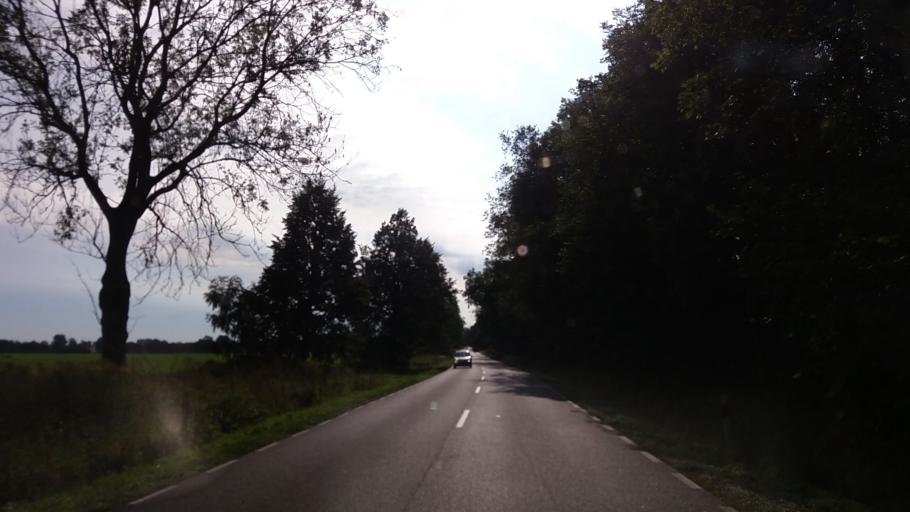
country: PL
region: West Pomeranian Voivodeship
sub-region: Powiat stargardzki
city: Suchan
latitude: 53.2144
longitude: 15.3115
